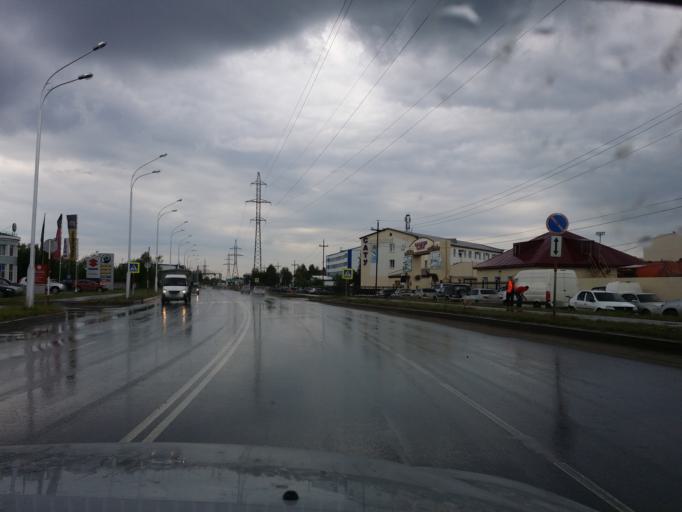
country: RU
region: Khanty-Mansiyskiy Avtonomnyy Okrug
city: Nizhnevartovsk
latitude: 60.9681
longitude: 76.5399
